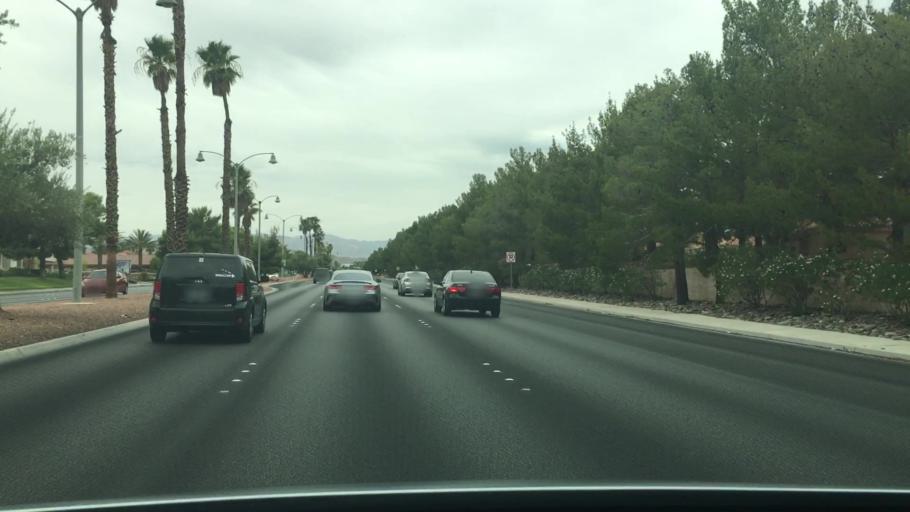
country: US
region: Nevada
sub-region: Clark County
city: Summerlin South
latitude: 36.1442
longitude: -115.2891
